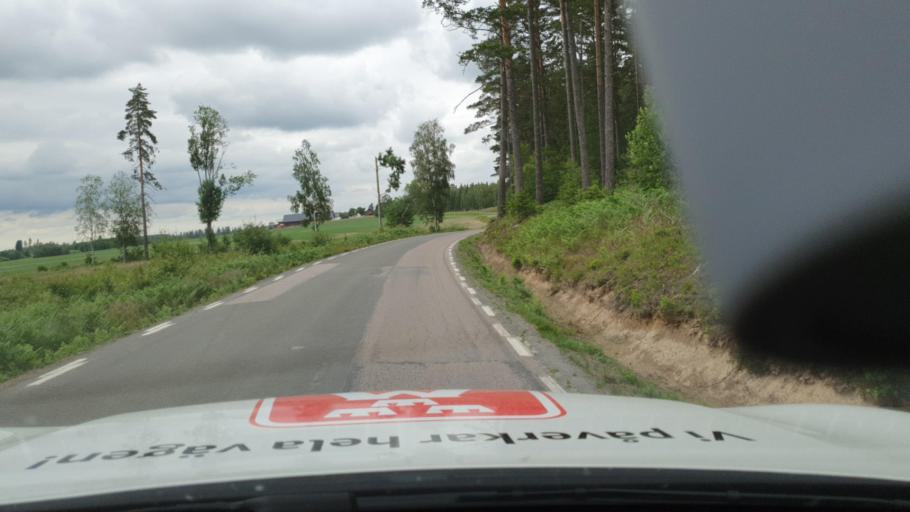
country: SE
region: Vaestra Goetaland
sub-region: Tidaholms Kommun
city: Olofstorp
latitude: 58.2689
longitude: 14.0993
